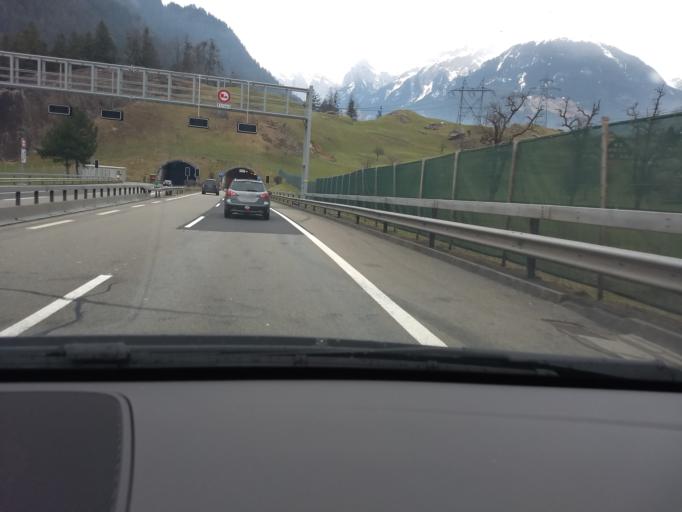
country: CH
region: Uri
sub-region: Uri
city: Silenen
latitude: 46.7559
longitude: 8.6487
